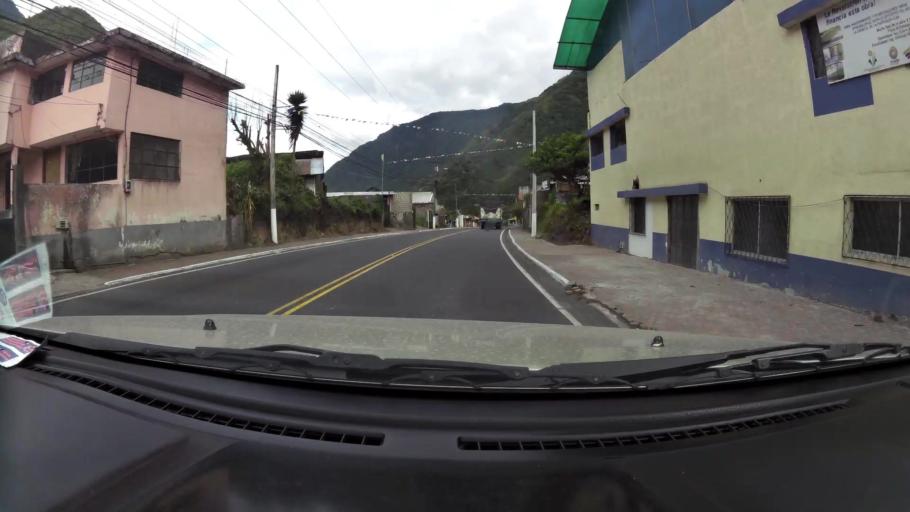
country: EC
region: Tungurahua
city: Banos
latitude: -1.3955
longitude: -78.3882
